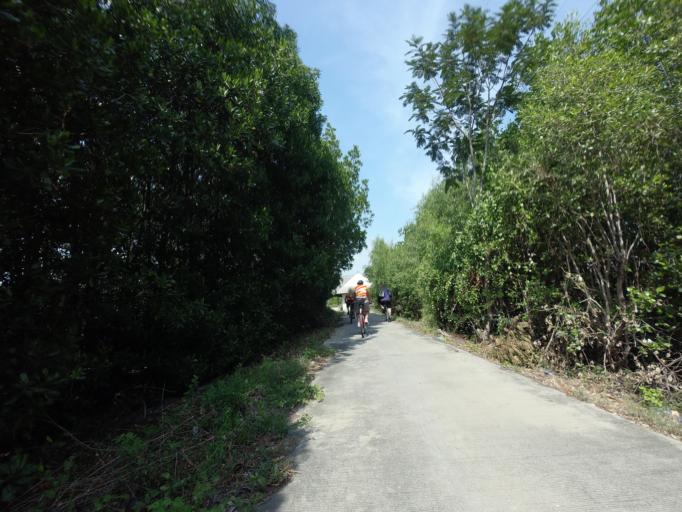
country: TH
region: Bangkok
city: Thung Khru
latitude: 13.5259
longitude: 100.4226
